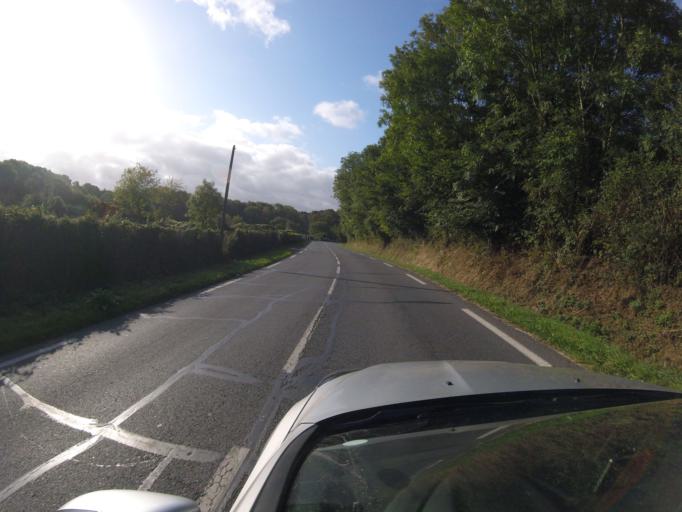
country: FR
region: Haute-Normandie
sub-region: Departement de la Seine-Maritime
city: Fecamp
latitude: 49.7658
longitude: 0.4046
